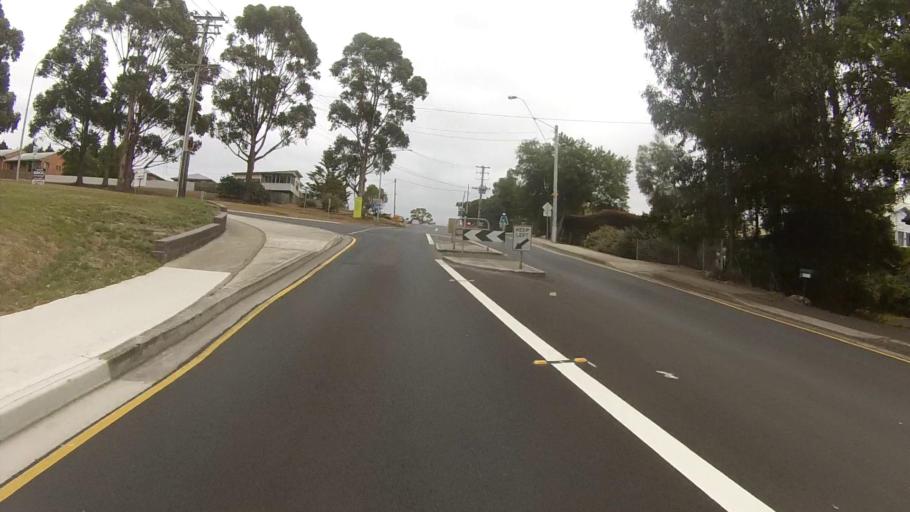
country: AU
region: Tasmania
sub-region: Kingborough
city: Kingston
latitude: -42.9693
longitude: 147.2905
